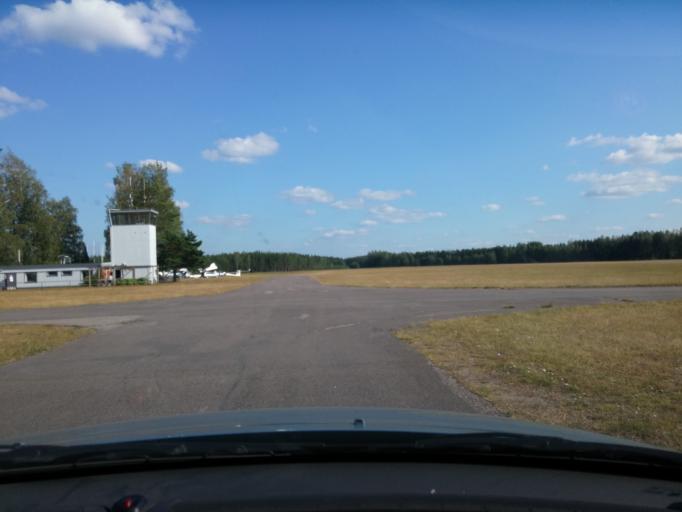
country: FI
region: Uusimaa
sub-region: Helsinki
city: Kaerkoelae
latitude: 60.7452
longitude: 24.1147
